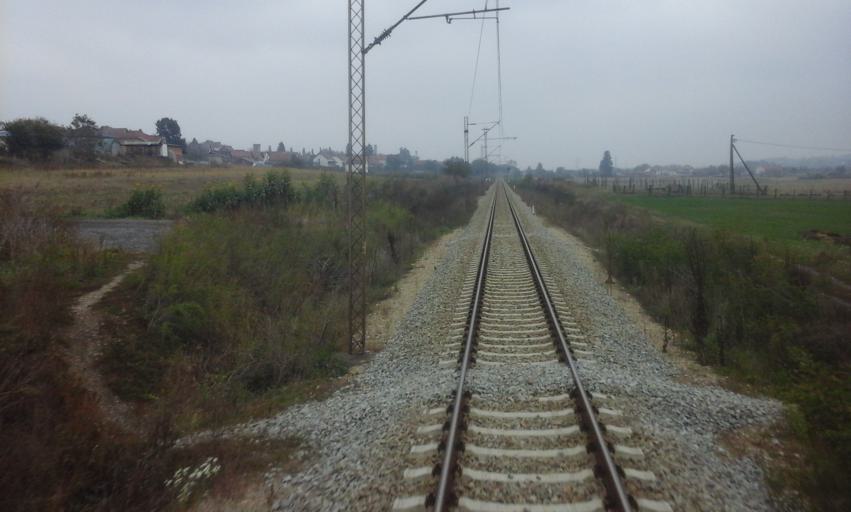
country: RS
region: Central Serbia
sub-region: Belgrade
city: Mladenovac
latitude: 44.4557
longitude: 20.6749
